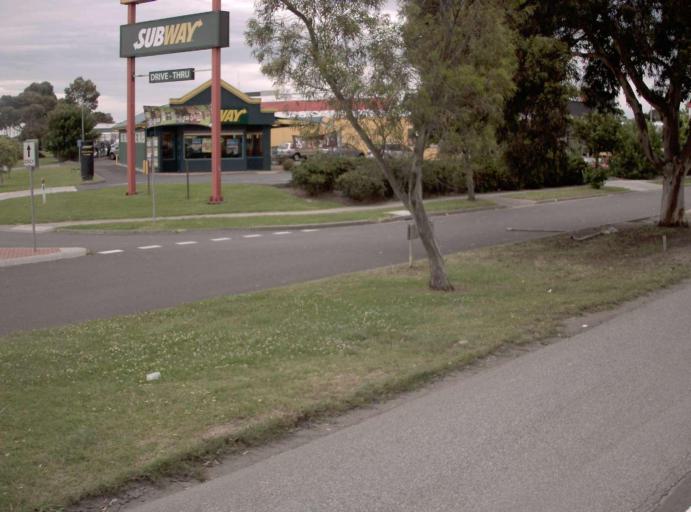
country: AU
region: Victoria
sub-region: Casey
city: Cranbourne
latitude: -38.1013
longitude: 145.2827
